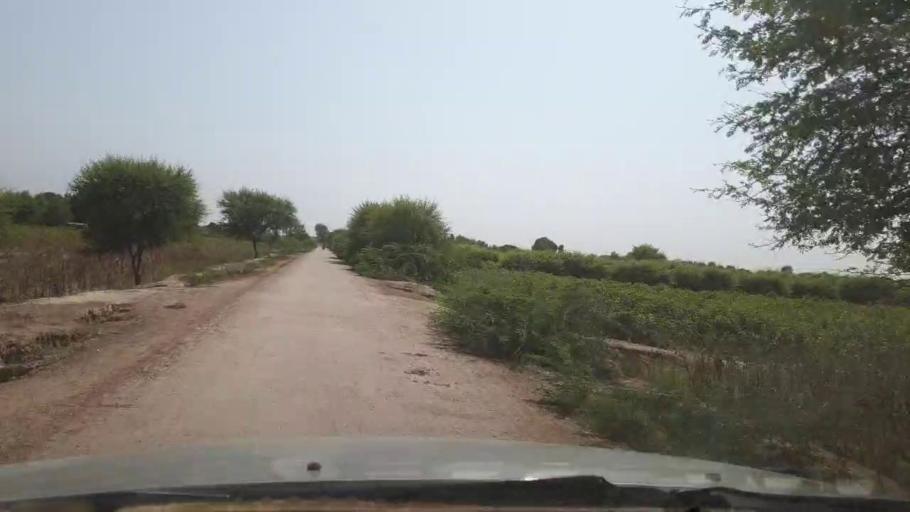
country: PK
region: Sindh
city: Tando Ghulam Ali
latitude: 25.1577
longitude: 68.8950
